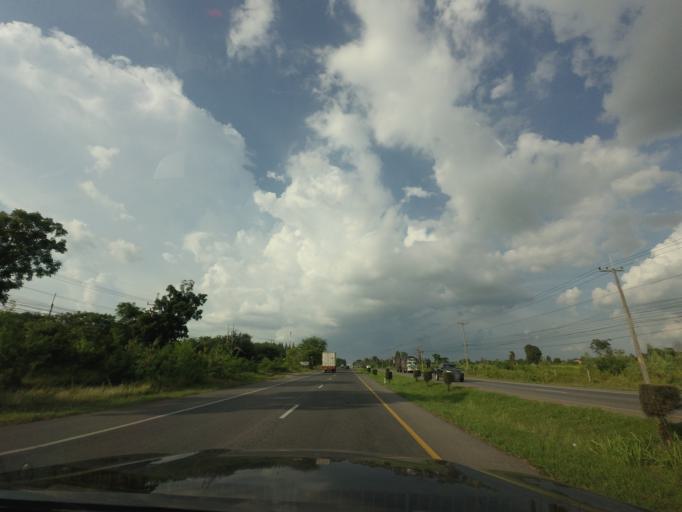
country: TH
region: Khon Kaen
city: Ban Haet
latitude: 16.2648
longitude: 102.7789
